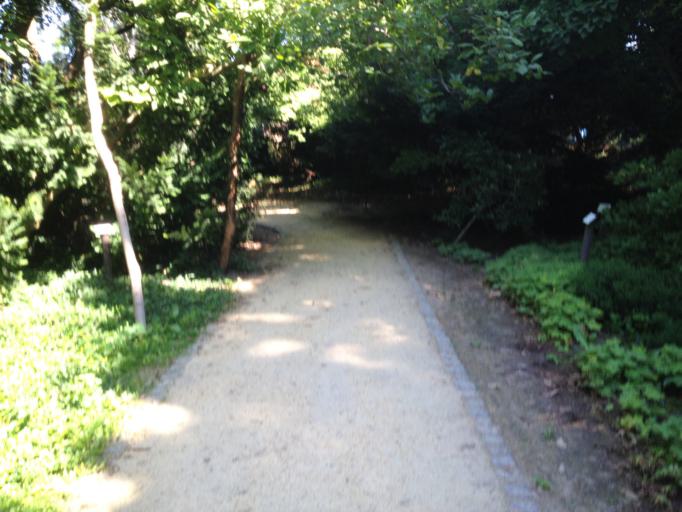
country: PL
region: Greater Poland Voivodeship
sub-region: Powiat poznanski
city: Kornik
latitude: 52.2454
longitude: 17.0952
